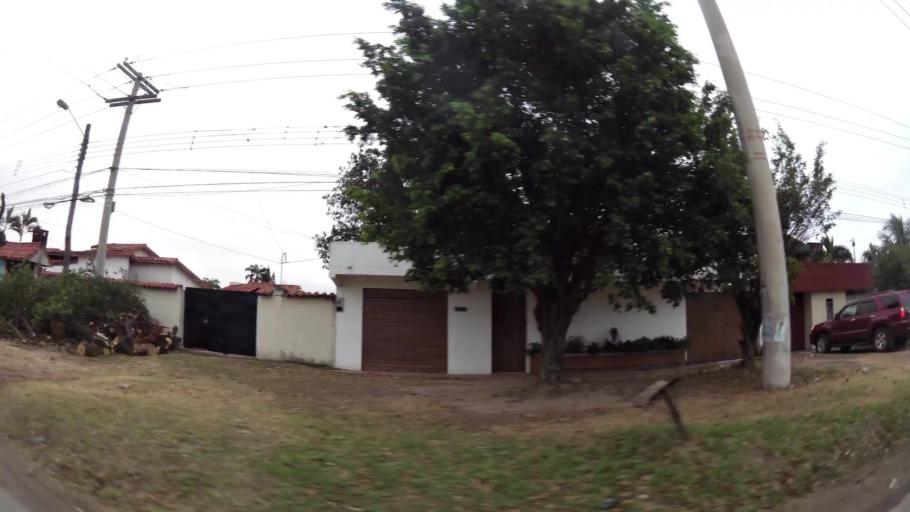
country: BO
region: Santa Cruz
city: Santa Cruz de la Sierra
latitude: -17.8107
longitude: -63.1777
